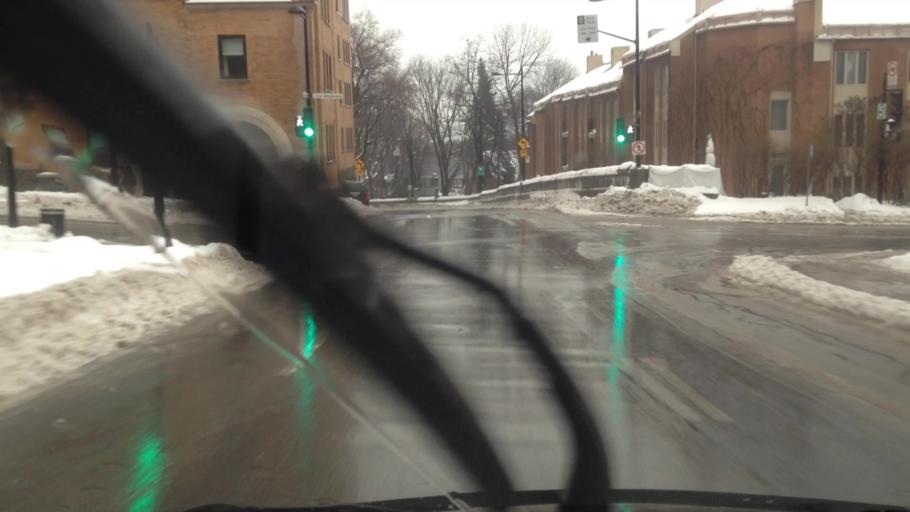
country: CA
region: Quebec
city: Westmount
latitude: 45.4951
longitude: -73.5967
